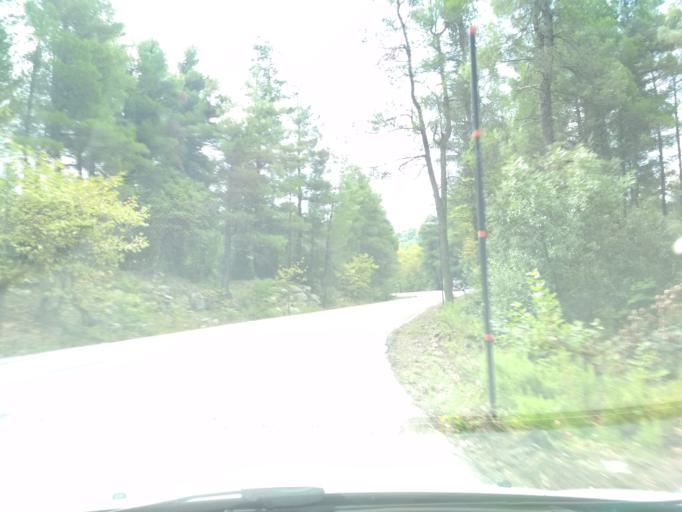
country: GR
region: Central Greece
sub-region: Nomos Evvoias
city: Politika
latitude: 38.6655
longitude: 23.5573
